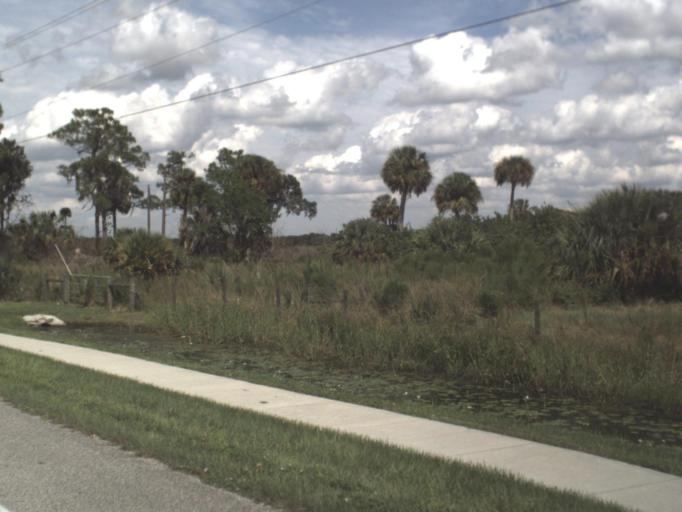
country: US
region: Florida
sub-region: Collier County
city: Immokalee
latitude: 26.5394
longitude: -81.4354
